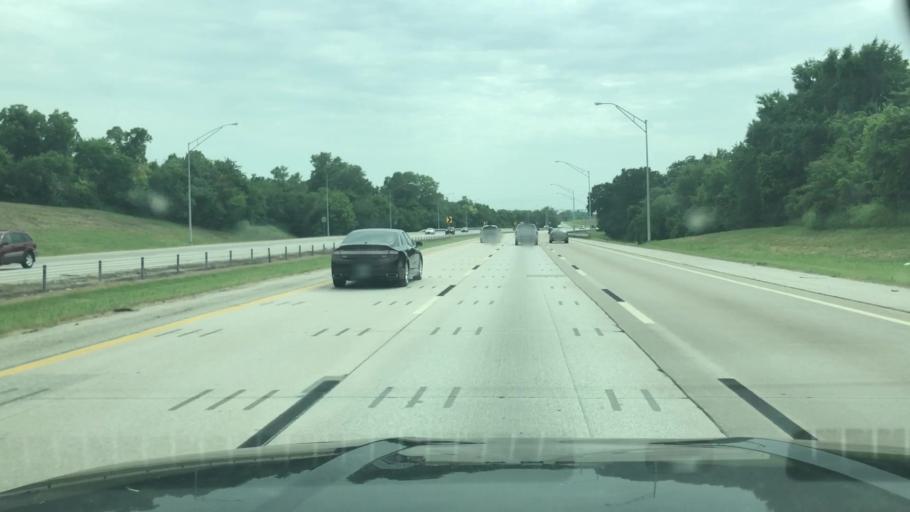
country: US
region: Oklahoma
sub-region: Tulsa County
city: Sand Springs
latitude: 36.1558
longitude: -96.0590
